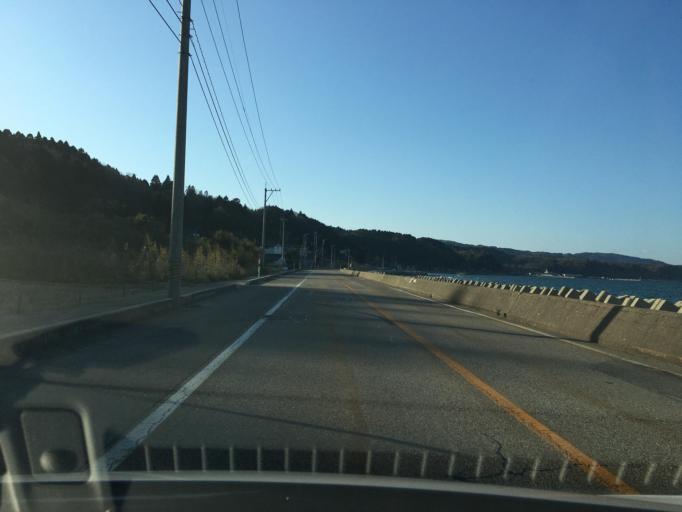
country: JP
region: Ishikawa
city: Nanao
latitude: 36.9959
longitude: 137.0522
